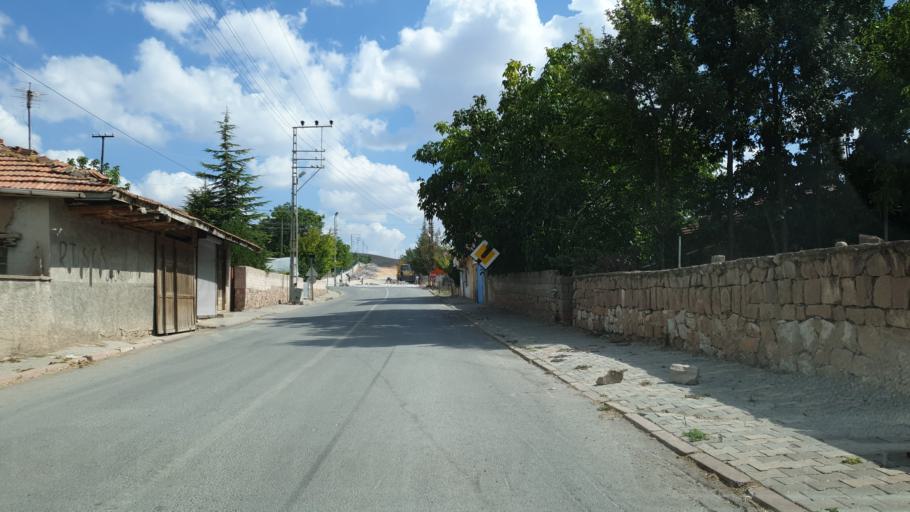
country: TR
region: Kayseri
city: Felahiye
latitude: 39.0892
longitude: 35.5638
